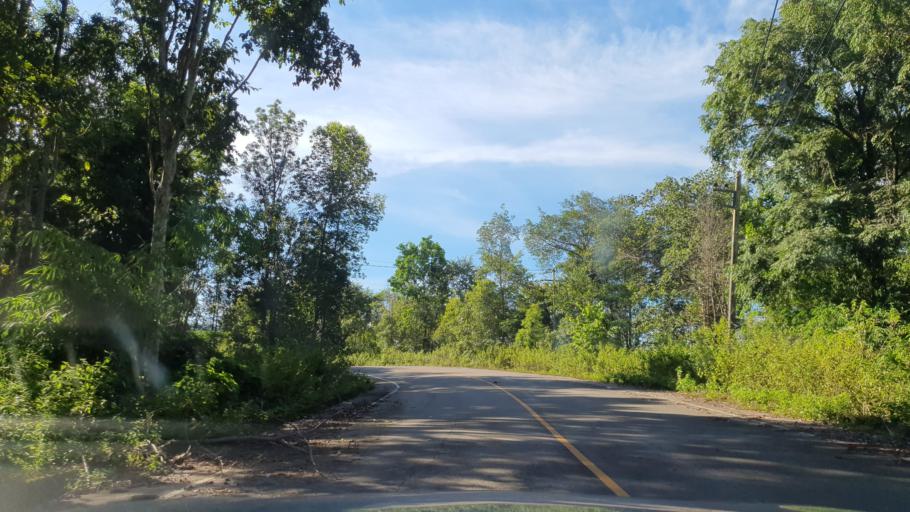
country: TH
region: Chiang Mai
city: Mae On
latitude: 18.7945
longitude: 99.3022
